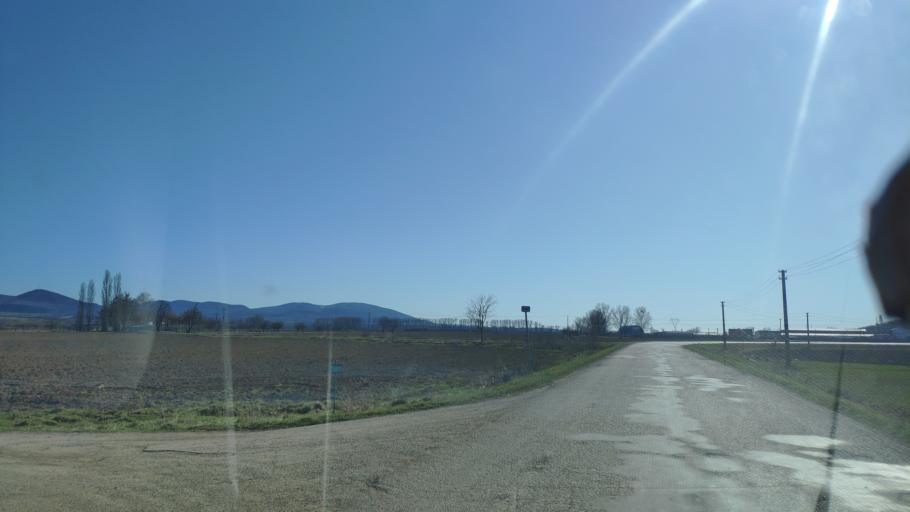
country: HU
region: Borsod-Abauj-Zemplen
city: Gonc
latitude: 48.5898
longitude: 21.3115
